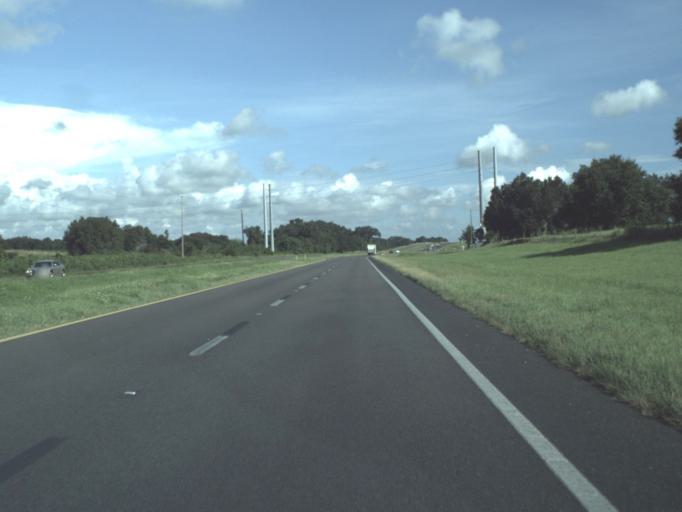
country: US
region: Florida
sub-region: Polk County
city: Fort Meade
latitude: 27.8073
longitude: -81.8193
